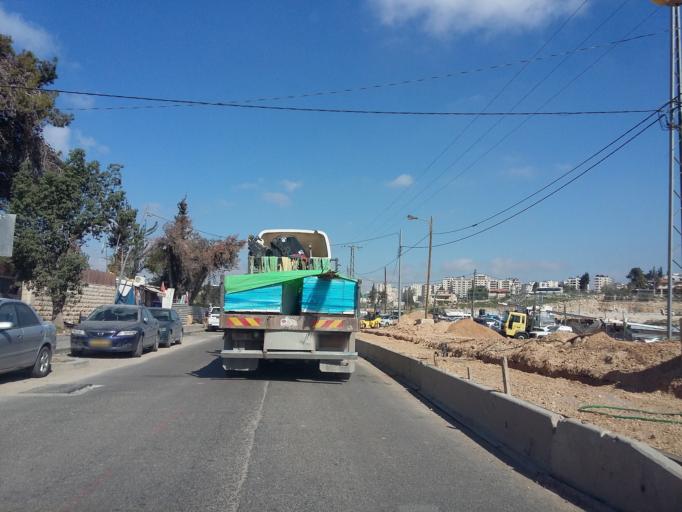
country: PS
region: West Bank
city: Qalandiya
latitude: 31.8585
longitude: 35.2222
